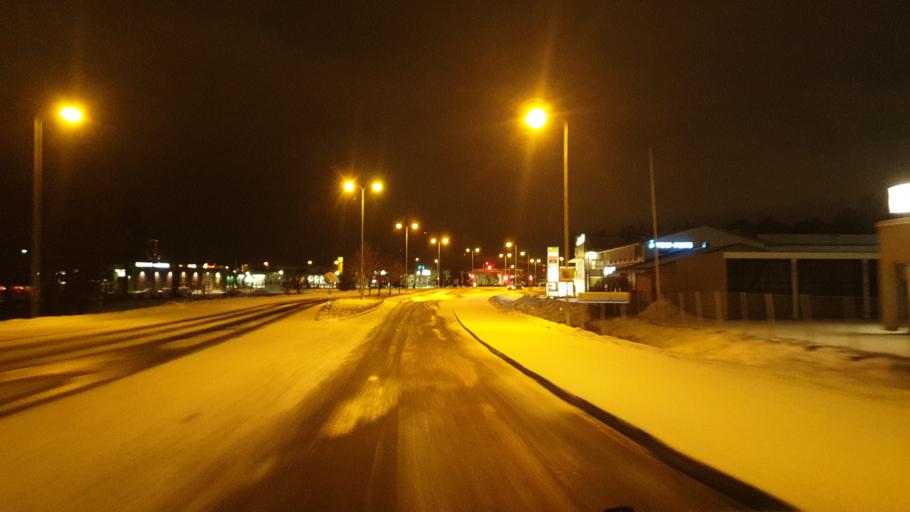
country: FI
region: Northern Ostrobothnia
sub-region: Oulu
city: Oulu
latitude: 64.9904
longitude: 25.4669
